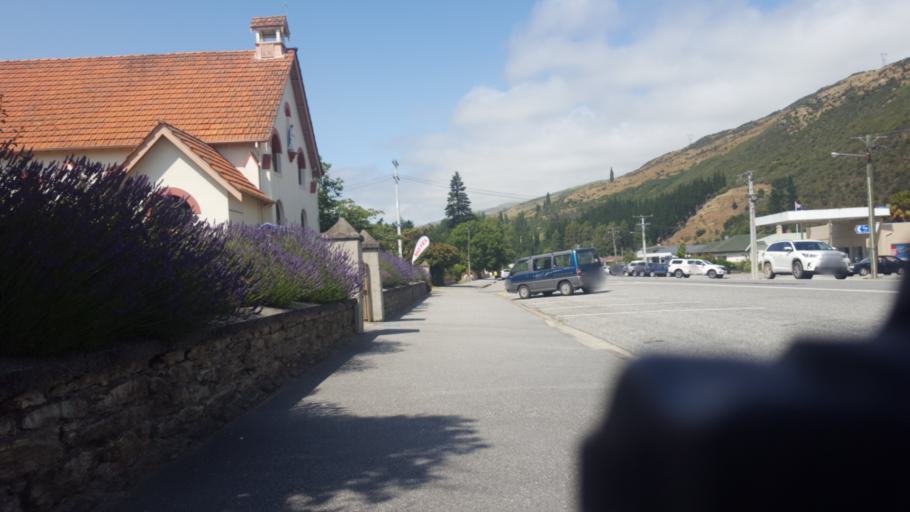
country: NZ
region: Otago
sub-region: Queenstown-Lakes District
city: Kingston
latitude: -45.5425
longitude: 169.3151
